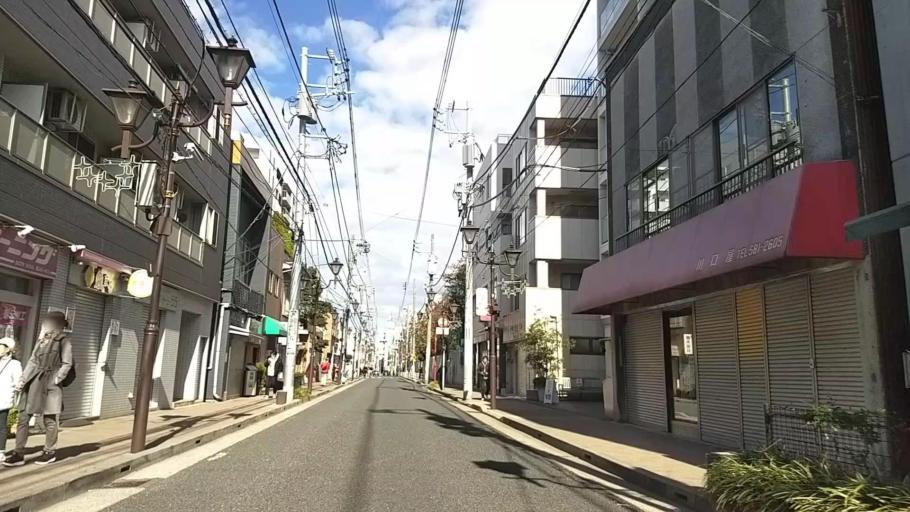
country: JP
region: Kanagawa
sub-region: Kawasaki-shi
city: Kawasaki
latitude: 35.5113
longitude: 139.6746
